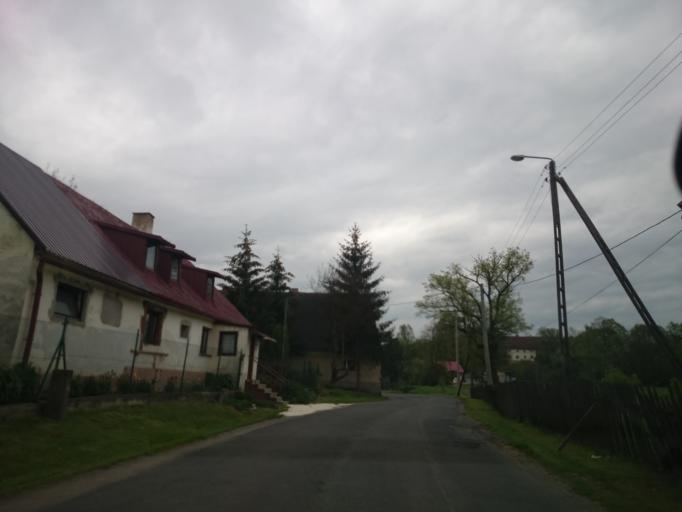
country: PL
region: Lower Silesian Voivodeship
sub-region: Powiat klodzki
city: Klodzko
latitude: 50.4141
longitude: 16.6962
